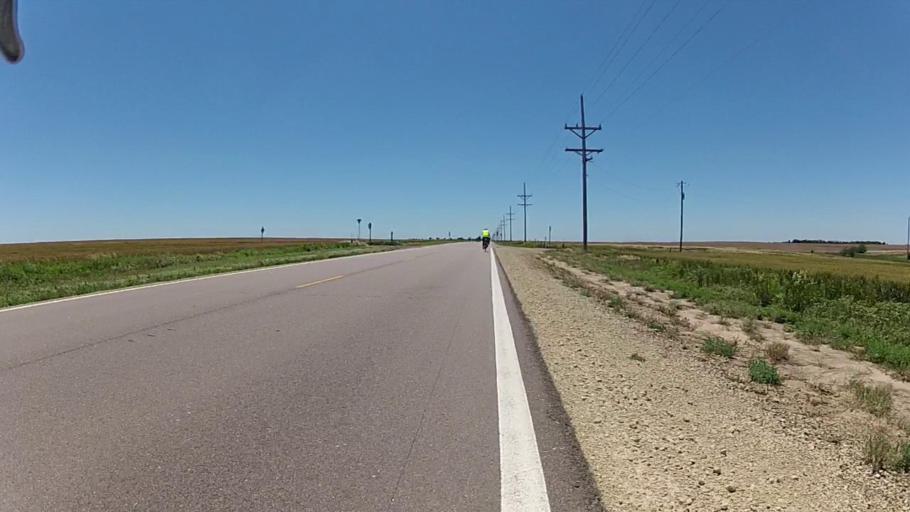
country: US
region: Kansas
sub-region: Kiowa County
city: Greensburg
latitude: 37.5284
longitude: -99.3207
